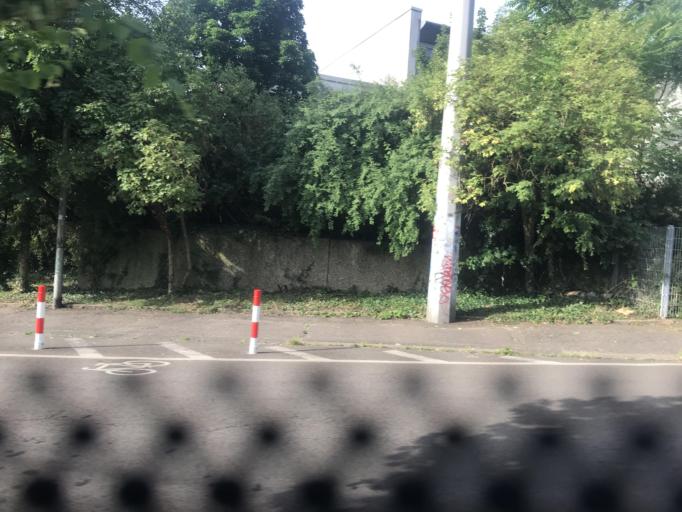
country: DE
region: Saarland
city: Saarbrucken
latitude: 49.2420
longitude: 6.9768
